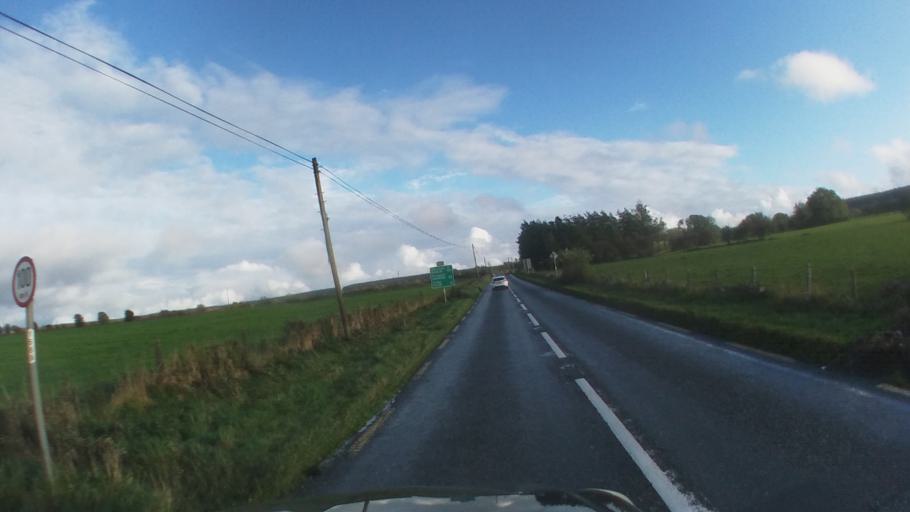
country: IE
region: Connaught
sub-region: Roscommon
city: Castlerea
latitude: 53.8293
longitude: -8.3662
